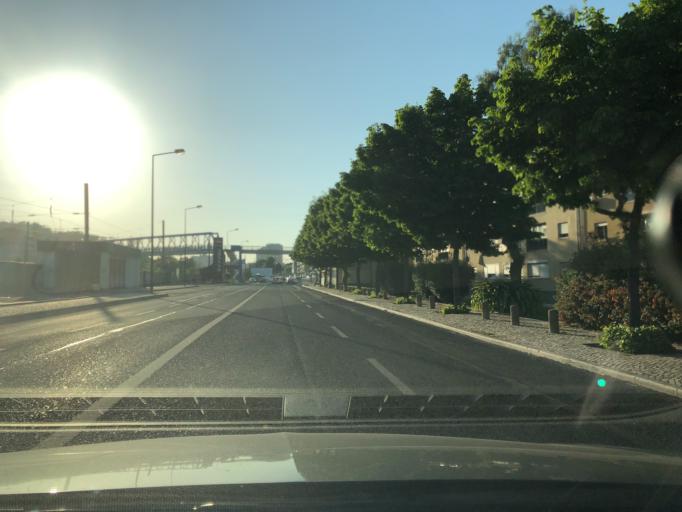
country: PT
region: Lisbon
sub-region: Odivelas
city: Pontinha
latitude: 38.7405
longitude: -9.1749
